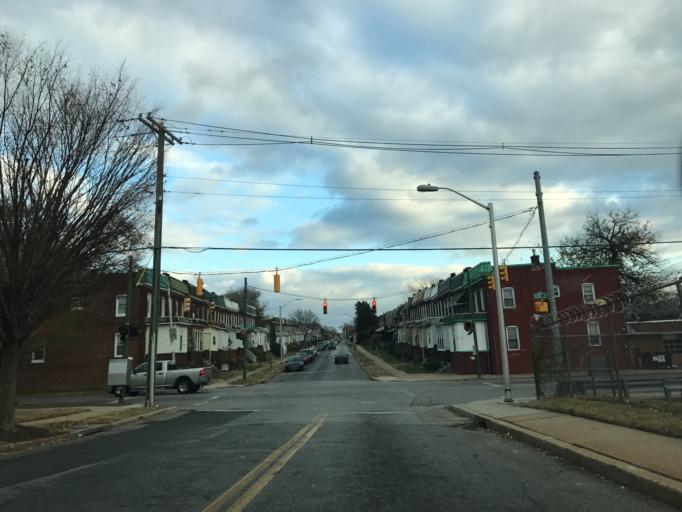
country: US
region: Maryland
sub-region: City of Baltimore
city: Baltimore
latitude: 39.3173
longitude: -76.6035
